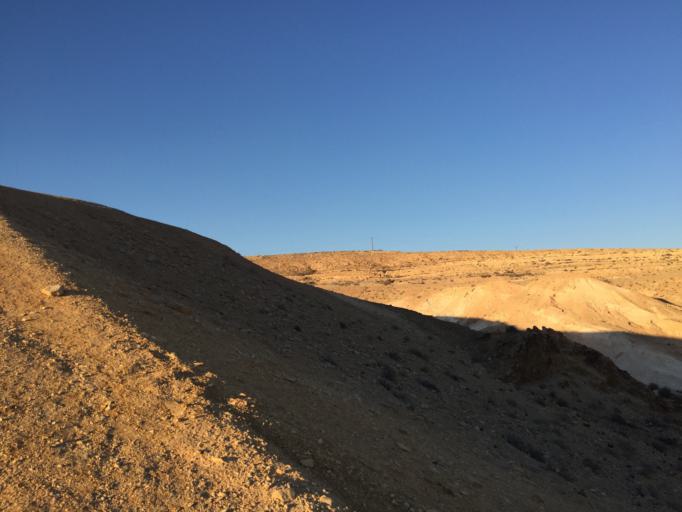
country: IL
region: Southern District
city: Midreshet Ben-Gurion
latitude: 30.8454
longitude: 34.7556
